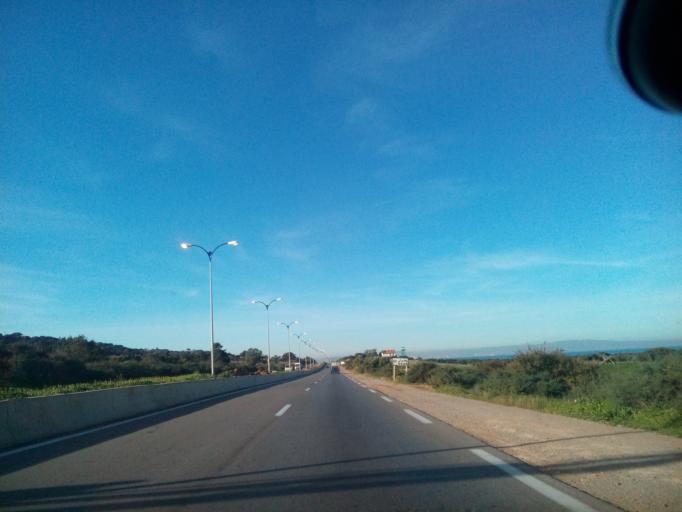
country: DZ
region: Mostaganem
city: Mostaganem
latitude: 35.8034
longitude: -0.0608
